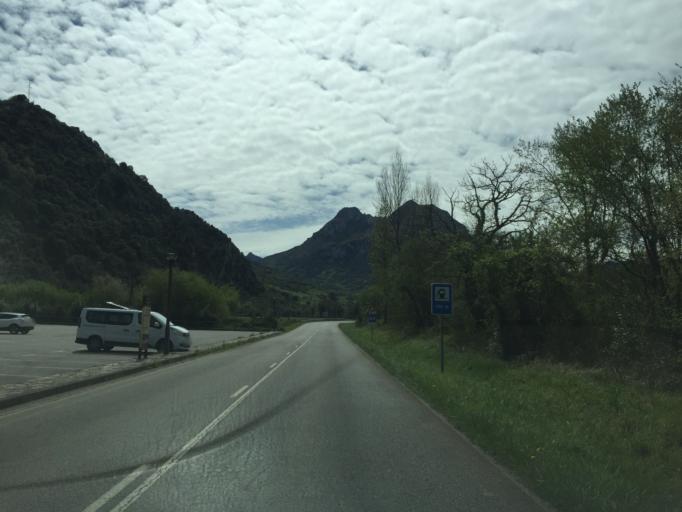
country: ES
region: Asturias
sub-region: Province of Asturias
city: Proaza
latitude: 43.2637
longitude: -6.0047
